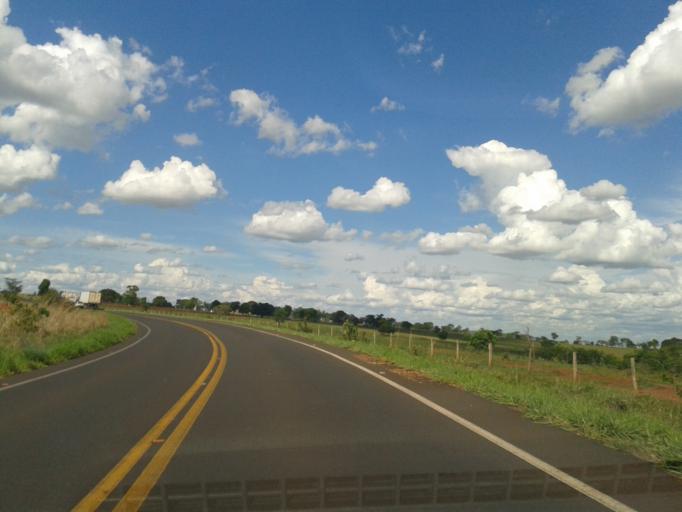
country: BR
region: Minas Gerais
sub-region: Iturama
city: Iturama
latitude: -19.6031
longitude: -50.0454
